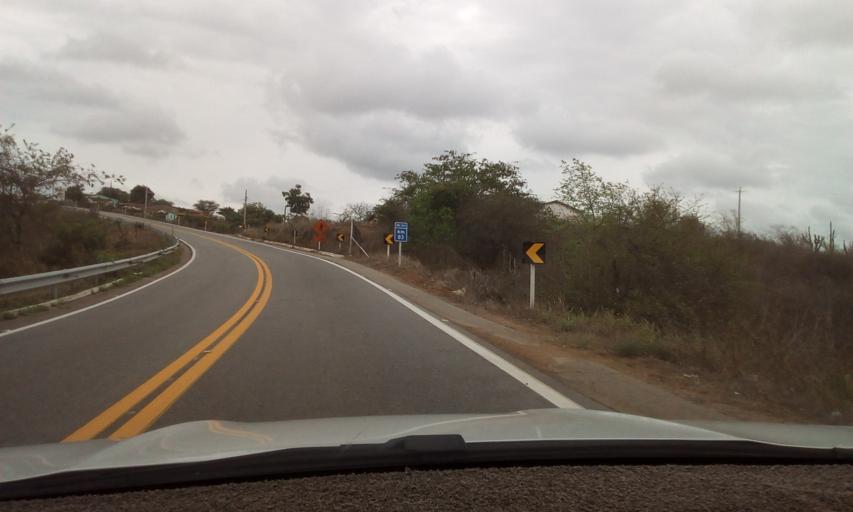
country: BR
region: Paraiba
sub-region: Areia
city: Remigio
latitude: -6.9413
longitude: -35.8226
